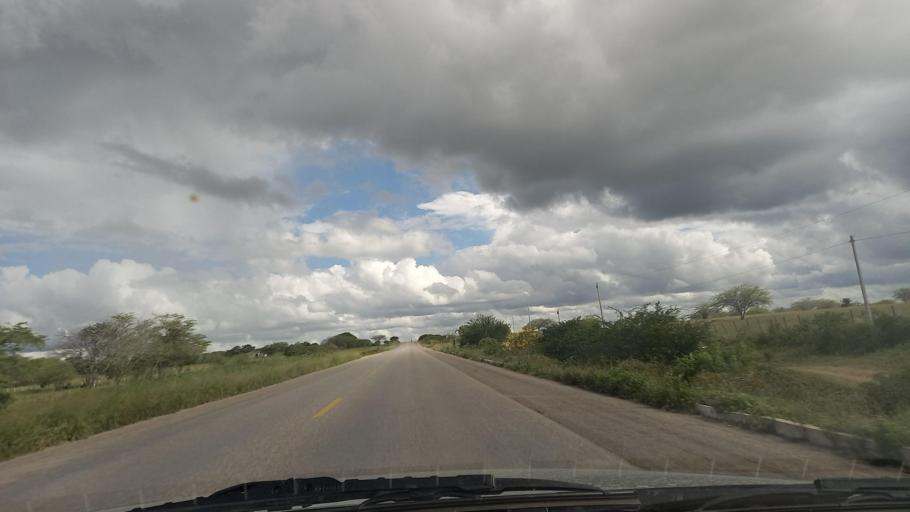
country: BR
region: Pernambuco
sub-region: Cachoeirinha
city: Cachoeirinha
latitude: -8.5168
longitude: -36.2555
